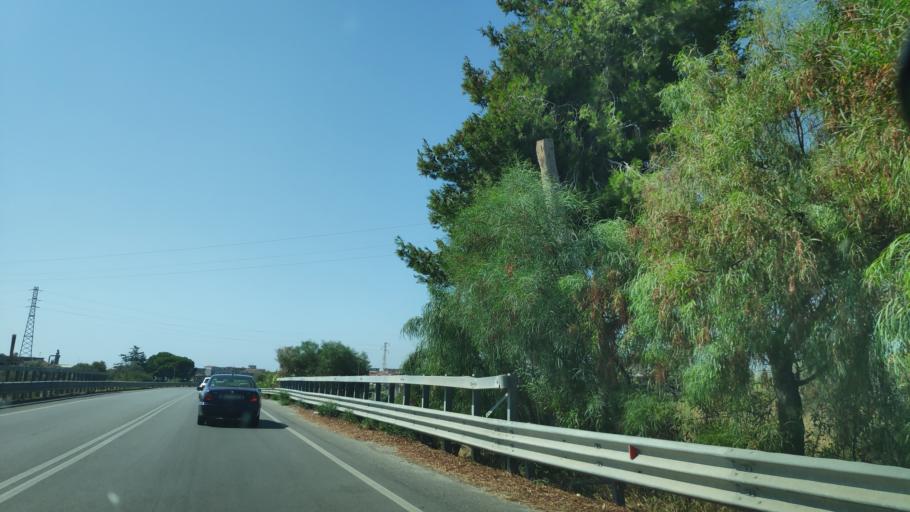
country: IT
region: Calabria
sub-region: Provincia di Reggio Calabria
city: Bovalino
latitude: 38.1465
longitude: 16.1682
